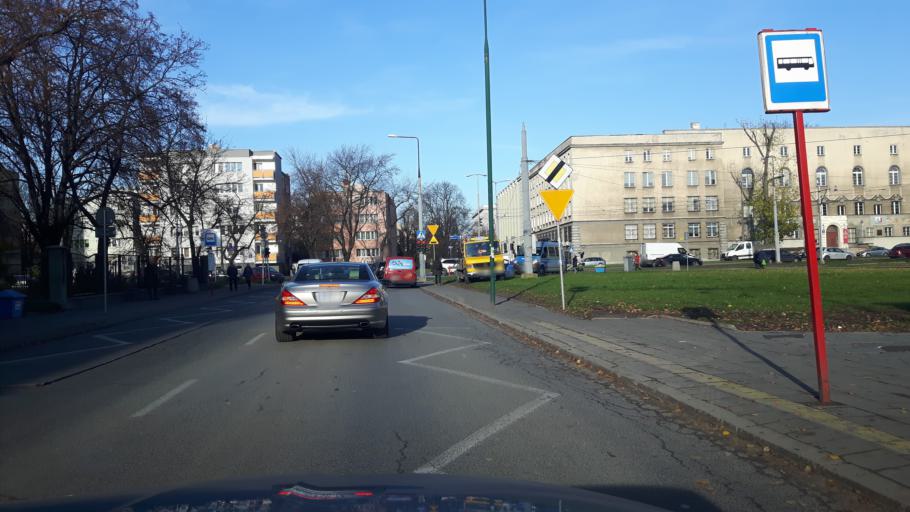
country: PL
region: Masovian Voivodeship
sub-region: Warszawa
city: Ochota
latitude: 52.2098
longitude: 20.9804
